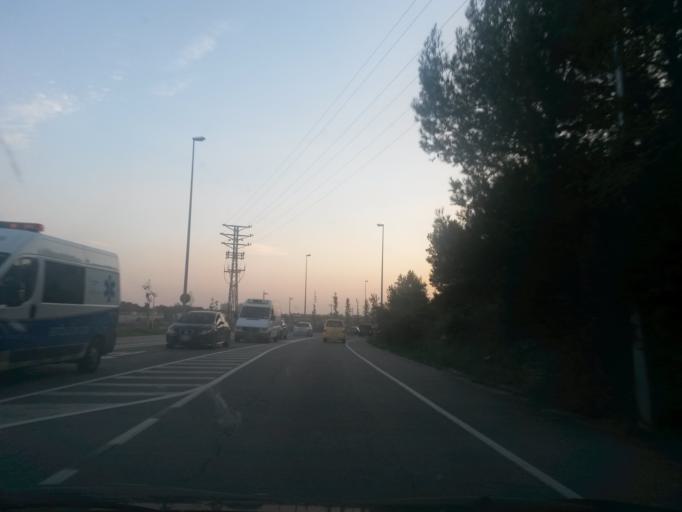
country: ES
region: Catalonia
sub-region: Provincia de Girona
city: Girona
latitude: 41.9966
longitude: 2.8160
